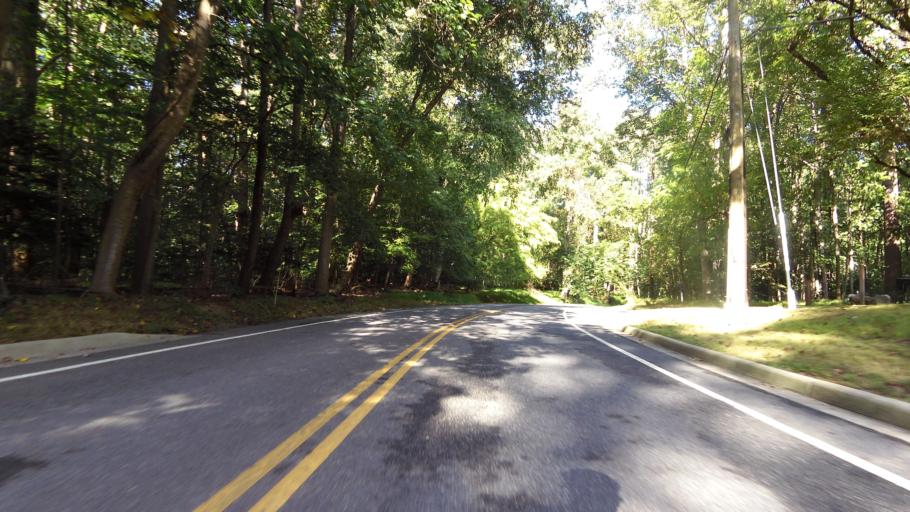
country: US
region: Maryland
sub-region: Montgomery County
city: Potomac
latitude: 38.9958
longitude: -77.2379
